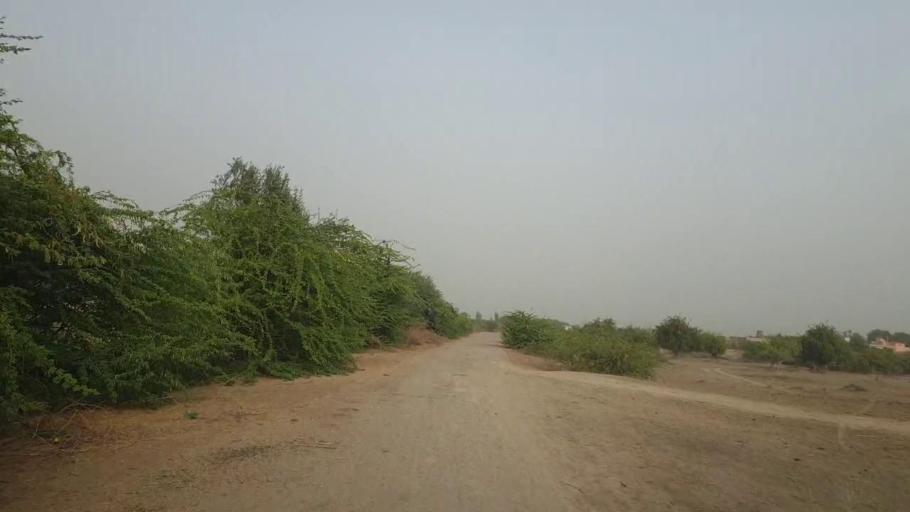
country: PK
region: Sindh
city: Kunri
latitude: 25.0749
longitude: 69.4333
